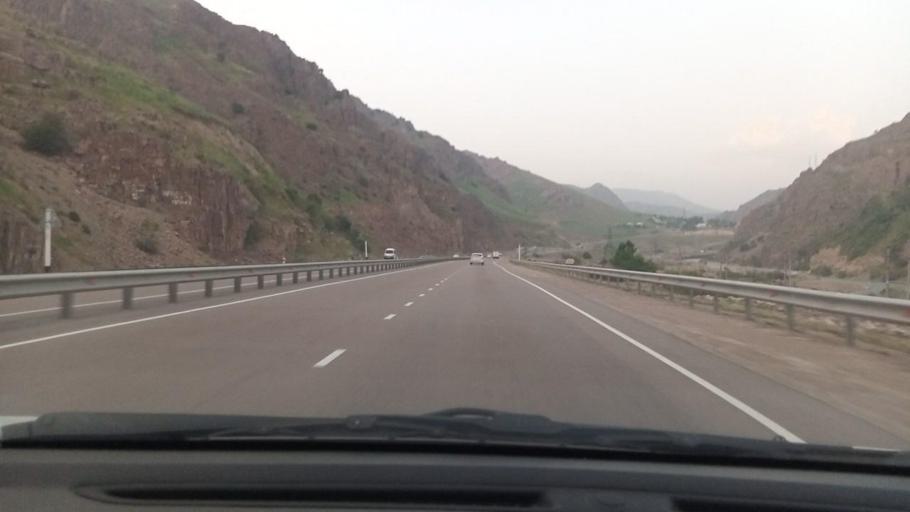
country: UZ
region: Toshkent
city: Angren
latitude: 41.1196
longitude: 70.3482
